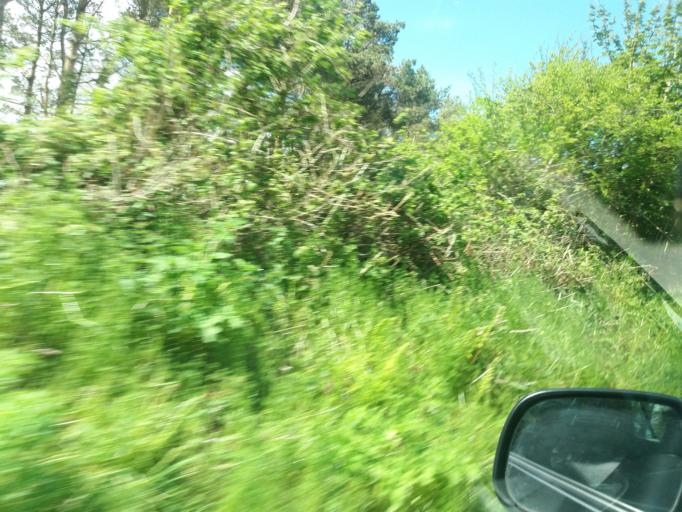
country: IE
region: Munster
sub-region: Waterford
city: Dunmore East
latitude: 52.2347
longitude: -6.9320
